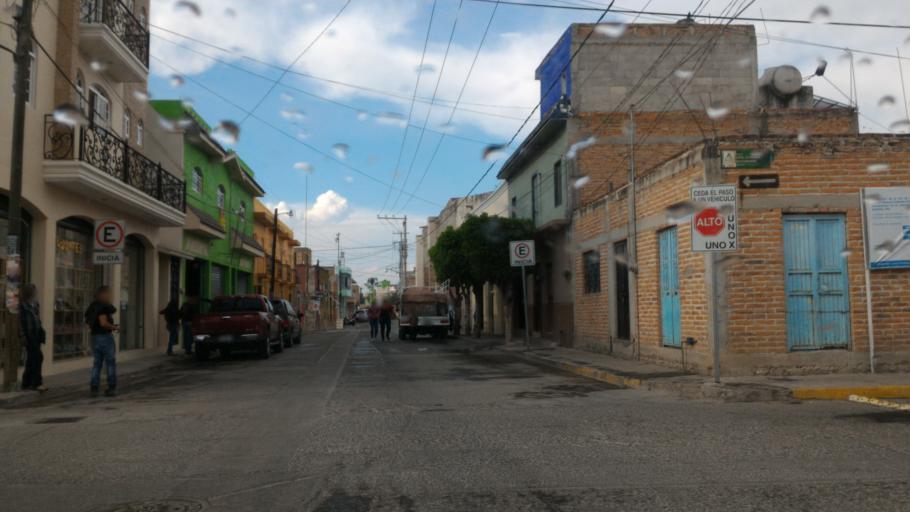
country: MX
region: Guanajuato
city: Ciudad Manuel Doblado
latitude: 20.7272
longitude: -101.9502
